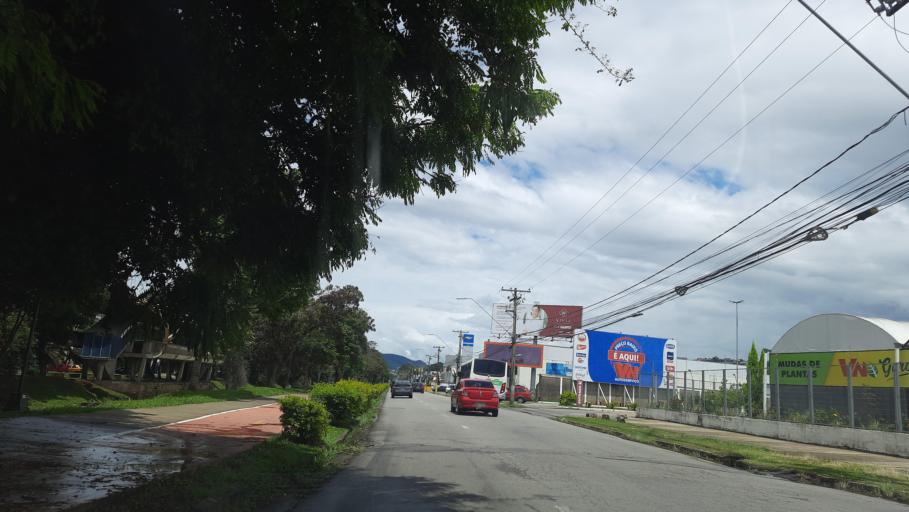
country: BR
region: Minas Gerais
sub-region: Pocos De Caldas
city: Pocos de Caldas
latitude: -21.7848
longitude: -46.5956
